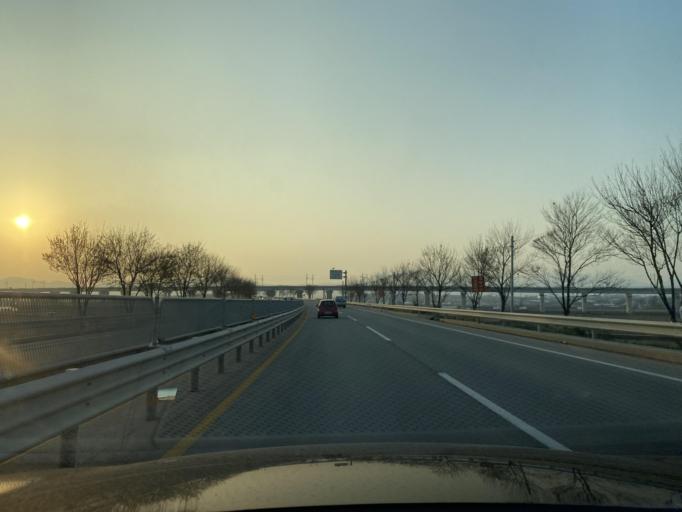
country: KR
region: Chungcheongnam-do
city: Hongsung
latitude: 36.6926
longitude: 126.7293
